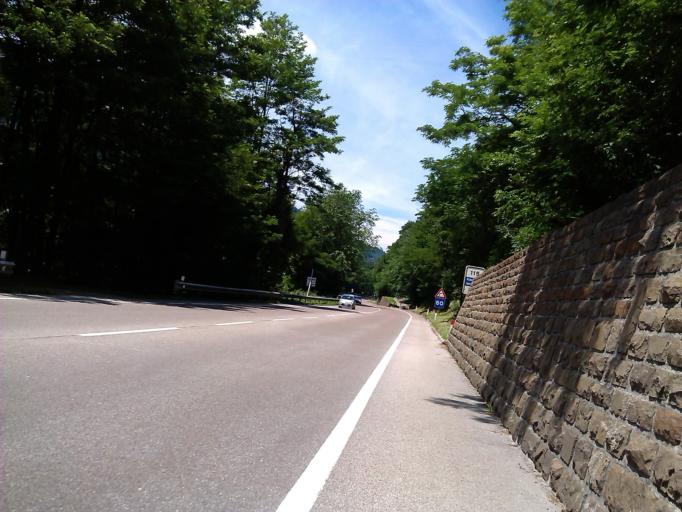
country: IT
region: Trentino-Alto Adige
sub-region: Provincia di Trento
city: Tenna
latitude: 46.0230
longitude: 11.2483
